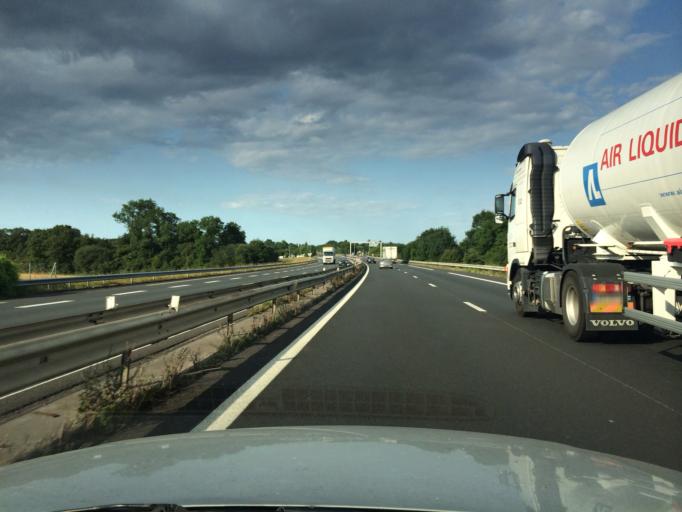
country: FR
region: Lower Normandy
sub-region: Departement du Calvados
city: Sannerville
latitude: 49.1749
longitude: -0.2063
